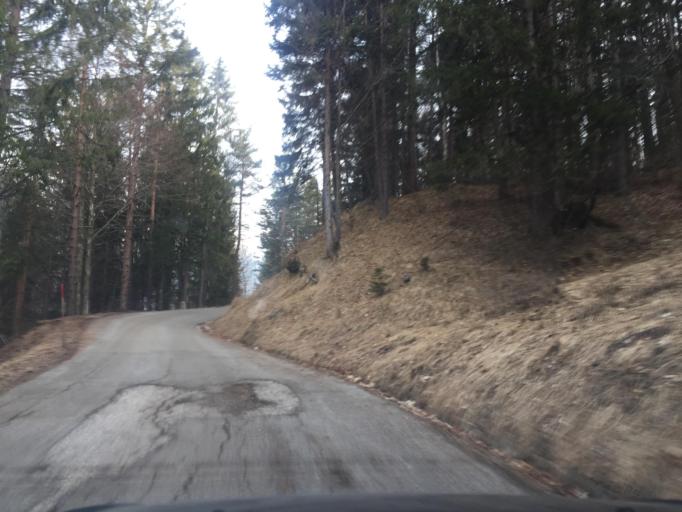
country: IT
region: Friuli Venezia Giulia
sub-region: Provincia di Udine
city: Tarvisio
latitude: 46.5042
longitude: 13.6383
